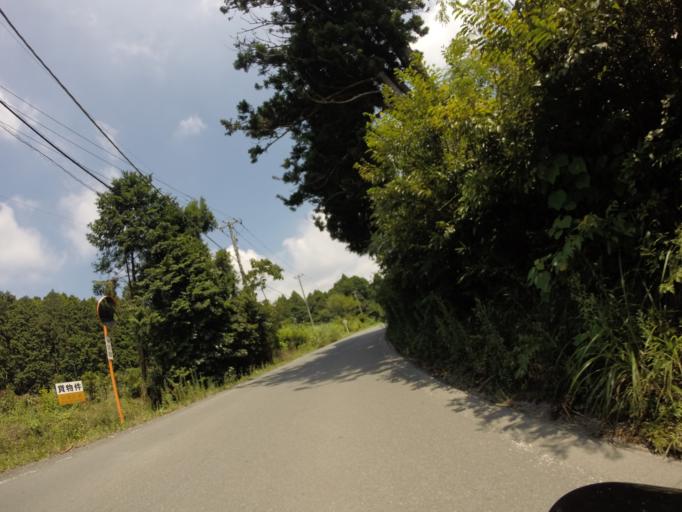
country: JP
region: Shizuoka
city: Fuji
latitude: 35.2324
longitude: 138.6916
